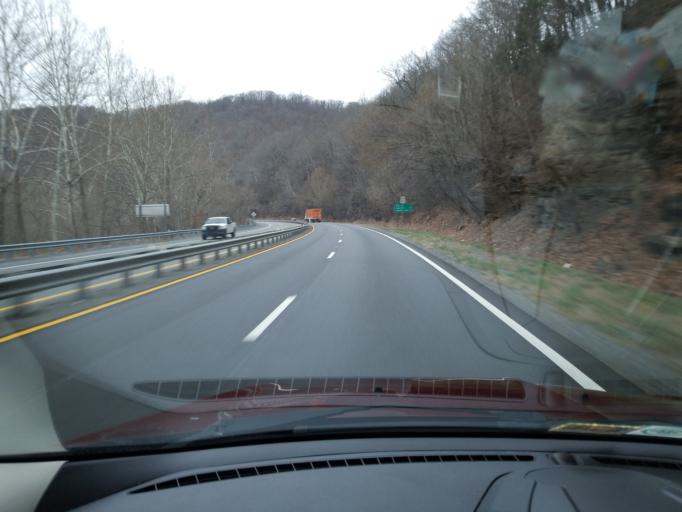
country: US
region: Virginia
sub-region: Giles County
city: Narrows
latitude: 37.3868
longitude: -80.8283
